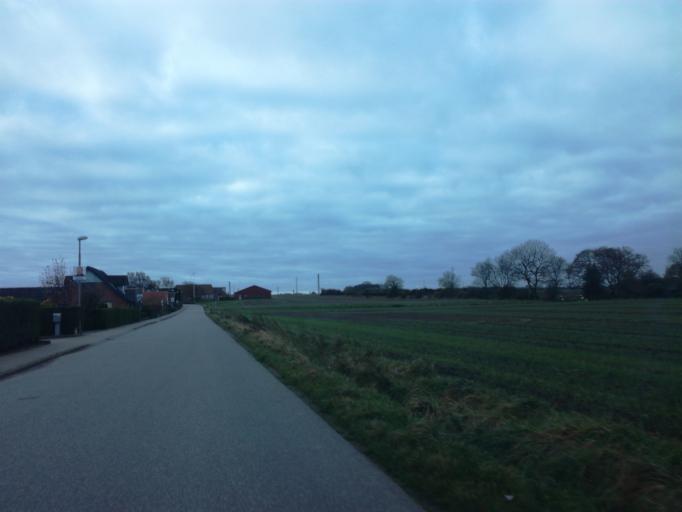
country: DK
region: South Denmark
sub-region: Fredericia Kommune
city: Fredericia
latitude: 55.6112
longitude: 9.7449
